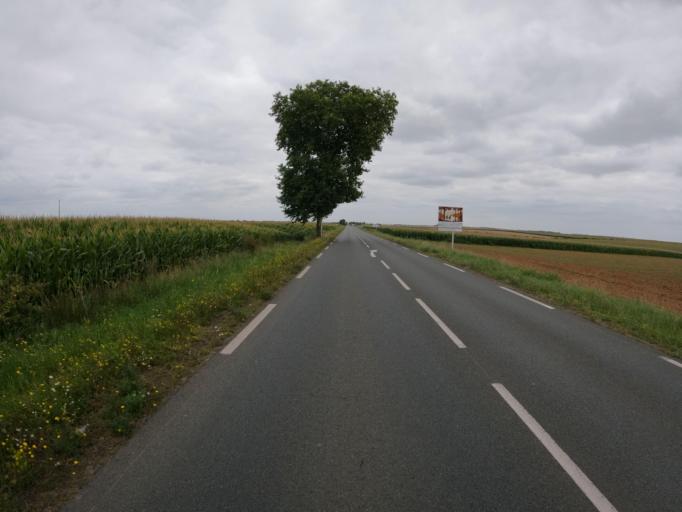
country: FR
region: Pays de la Loire
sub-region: Departement de la Vendee
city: Serigne
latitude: 46.4816
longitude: -0.8832
